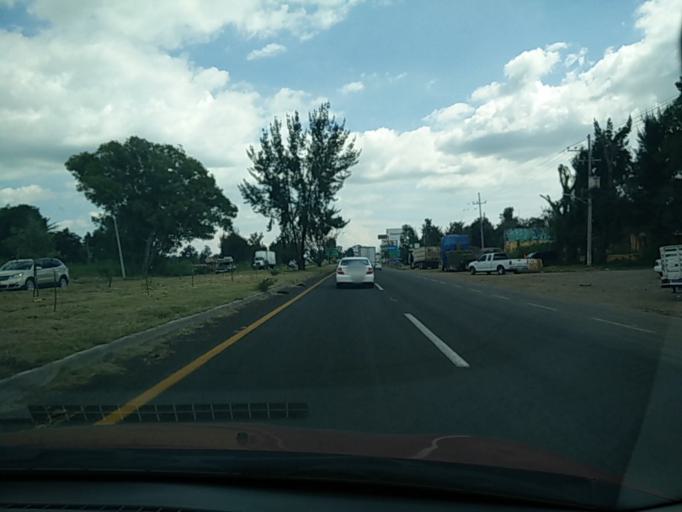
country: MX
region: Jalisco
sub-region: Tlajomulco de Zuniga
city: Rancho Alegre [Fraccionamiento]
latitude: 20.4587
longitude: -103.2532
